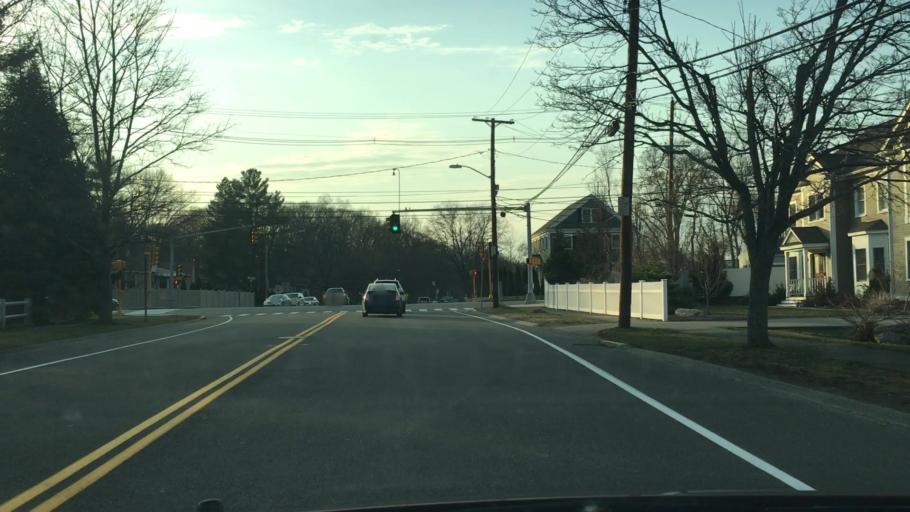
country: US
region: Massachusetts
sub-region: Middlesex County
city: Lexington
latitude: 42.4405
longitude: -71.2320
